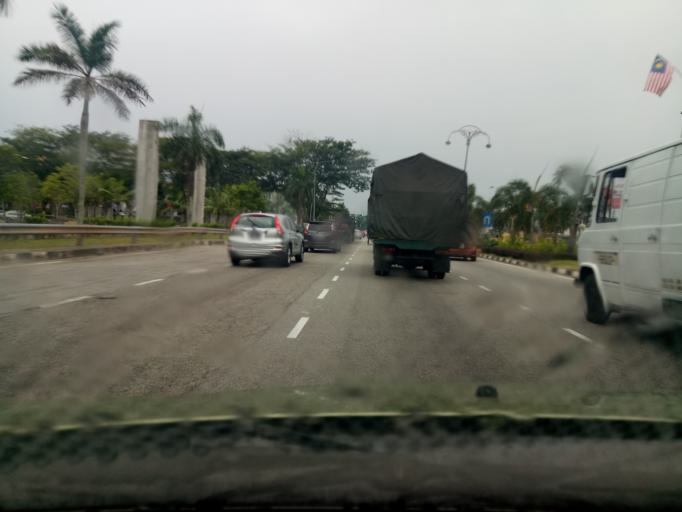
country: MY
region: Kedah
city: Sungai Petani
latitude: 5.6737
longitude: 100.5075
